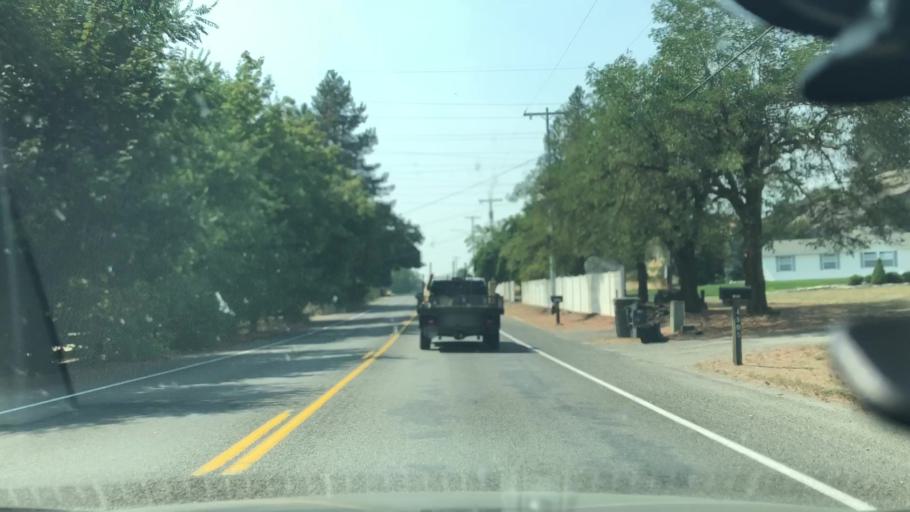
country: US
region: Washington
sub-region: Spokane County
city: Millwood
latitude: 47.6856
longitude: -117.3393
